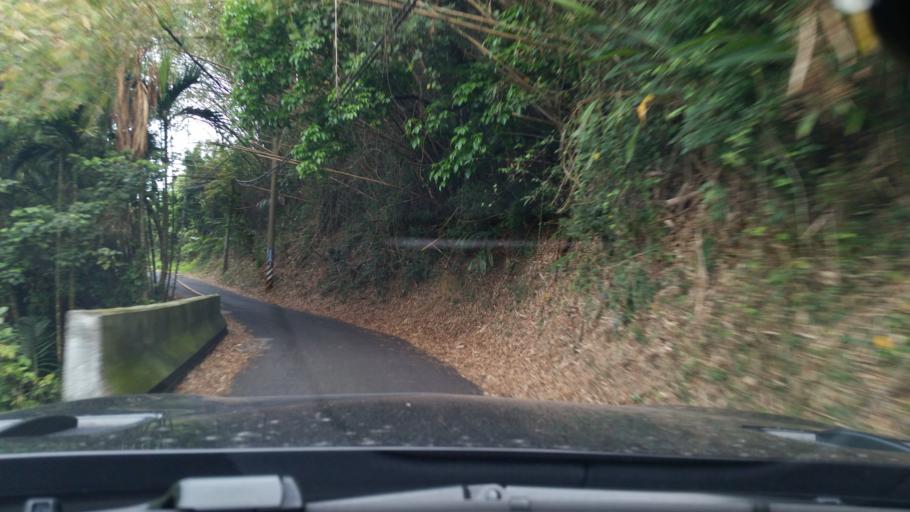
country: TW
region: Taiwan
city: Fengyuan
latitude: 24.3442
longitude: 120.7762
